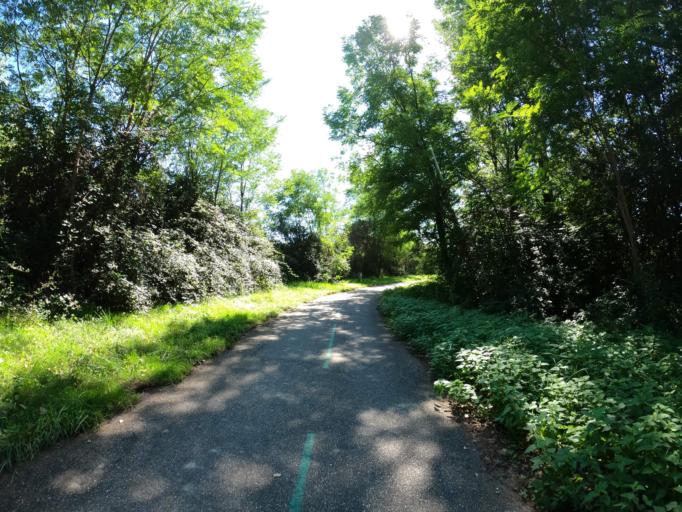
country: FR
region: Aquitaine
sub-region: Departement du Lot-et-Garonne
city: Bias
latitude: 44.4041
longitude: 0.6640
